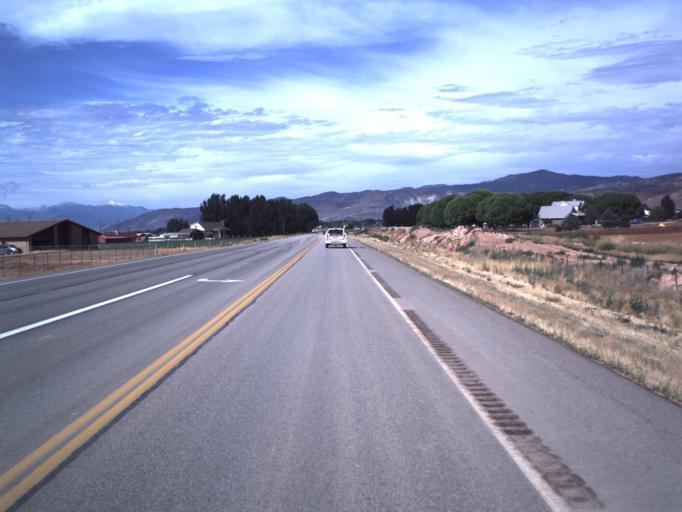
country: US
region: Utah
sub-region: Sevier County
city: Richfield
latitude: 38.7911
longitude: -112.0442
